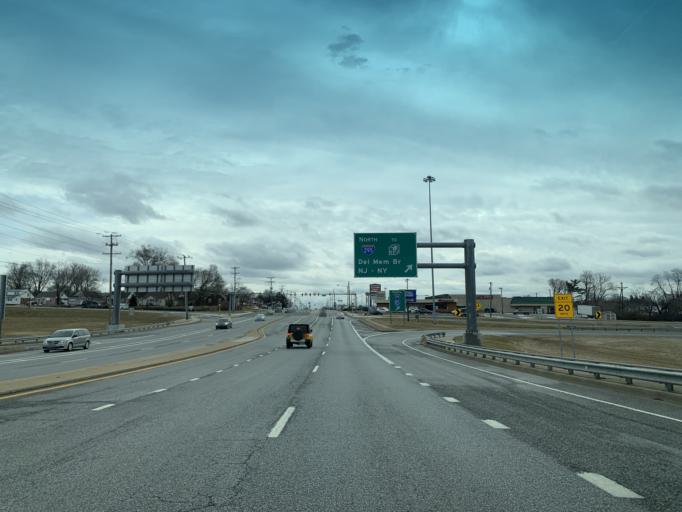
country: US
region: Delaware
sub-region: New Castle County
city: Wilmington Manor
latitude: 39.6950
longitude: -75.5541
